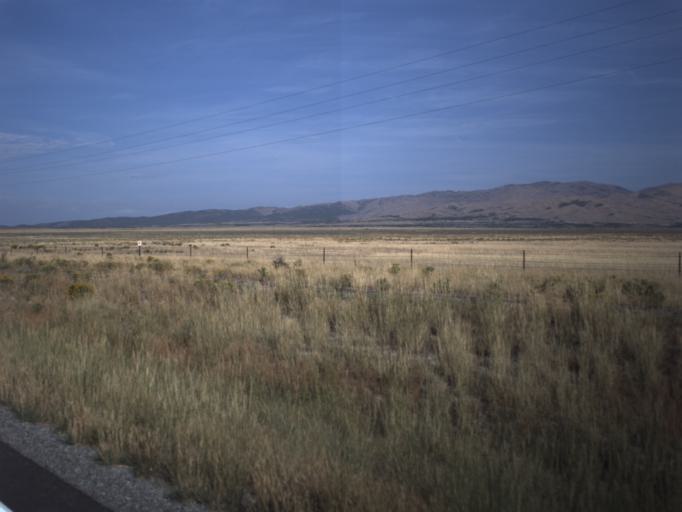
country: US
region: Idaho
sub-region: Oneida County
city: Malad City
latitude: 41.9658
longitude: -112.9970
